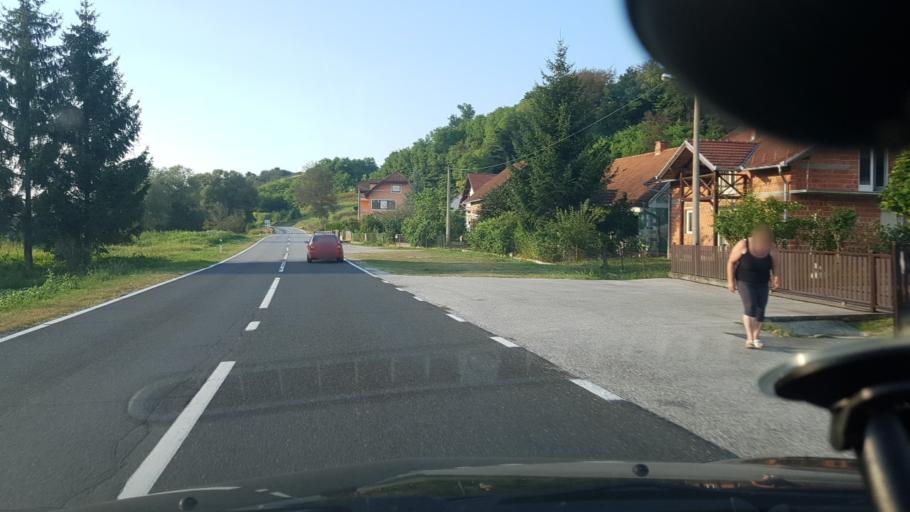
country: HR
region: Krapinsko-Zagorska
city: Pregrada
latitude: 46.1220
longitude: 15.8053
